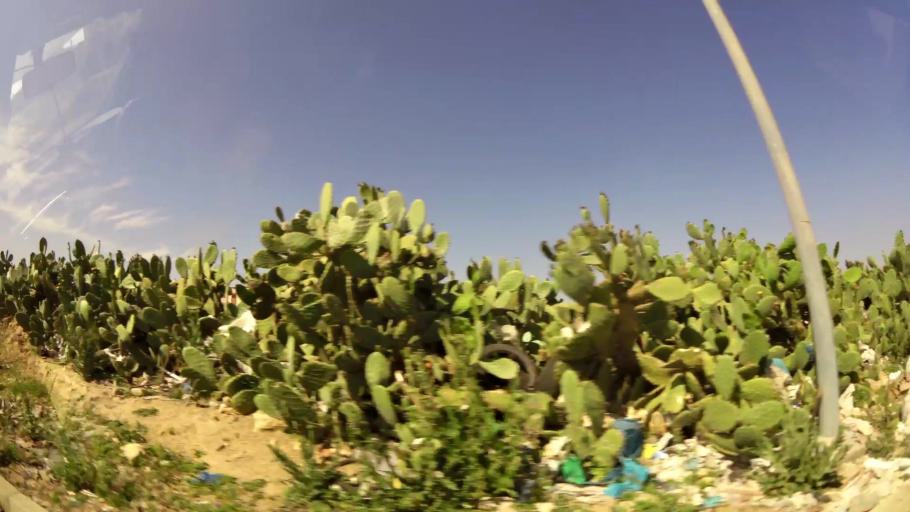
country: MA
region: Oriental
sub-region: Oujda-Angad
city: Oujda
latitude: 34.6976
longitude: -1.8763
